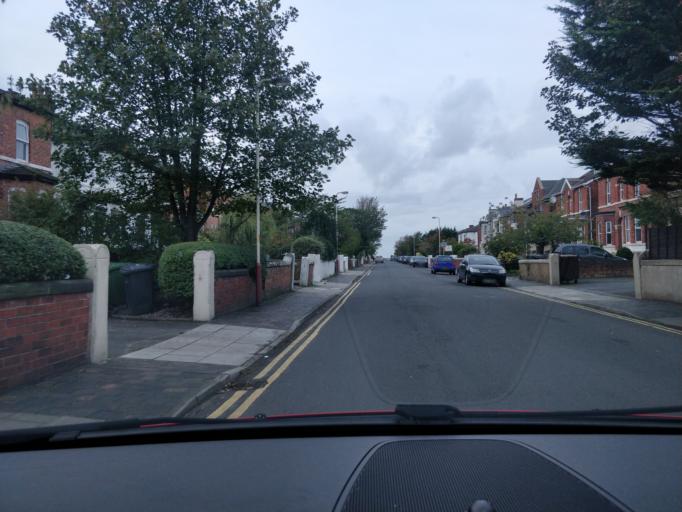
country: GB
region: England
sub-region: Sefton
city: Southport
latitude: 53.6536
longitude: -2.9978
